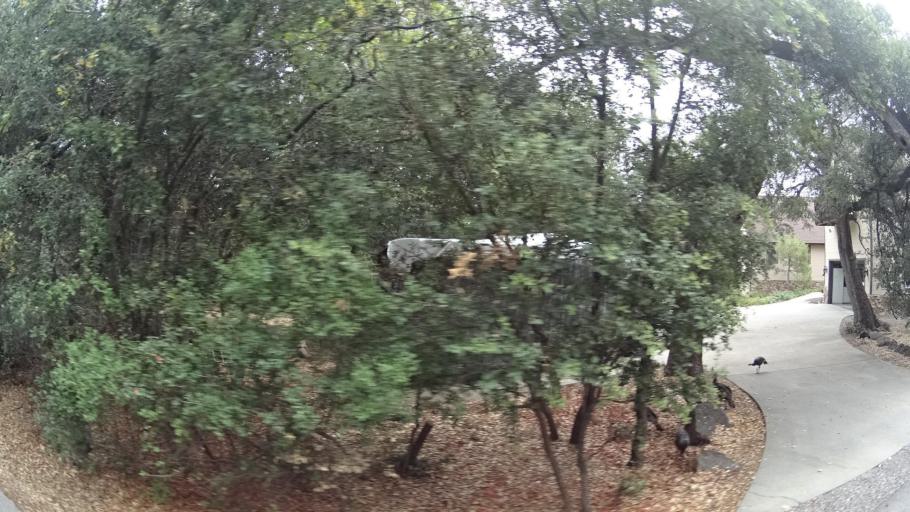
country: US
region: California
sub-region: San Diego County
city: Julian
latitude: 33.0458
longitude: -116.6264
